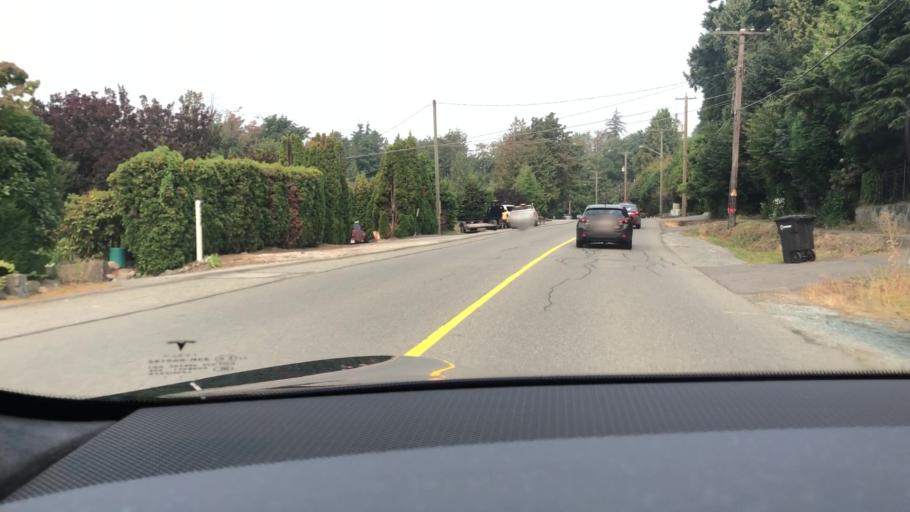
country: CA
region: British Columbia
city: Burnaby
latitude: 49.2084
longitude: -123.0023
